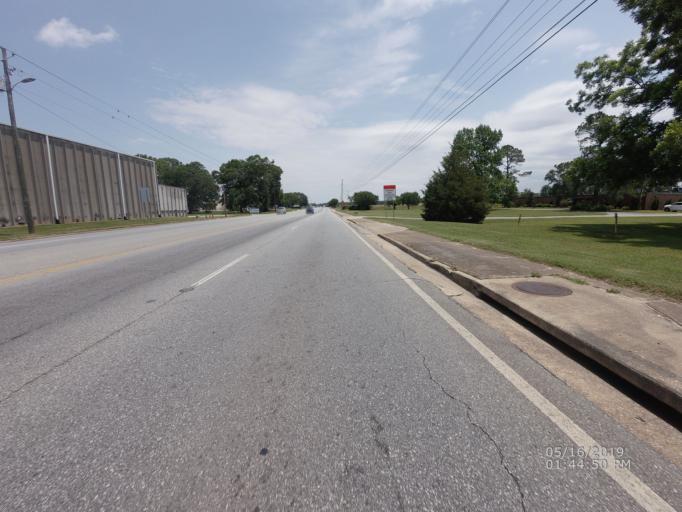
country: US
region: Georgia
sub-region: Dougherty County
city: Albany
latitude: 31.5490
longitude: -84.1854
